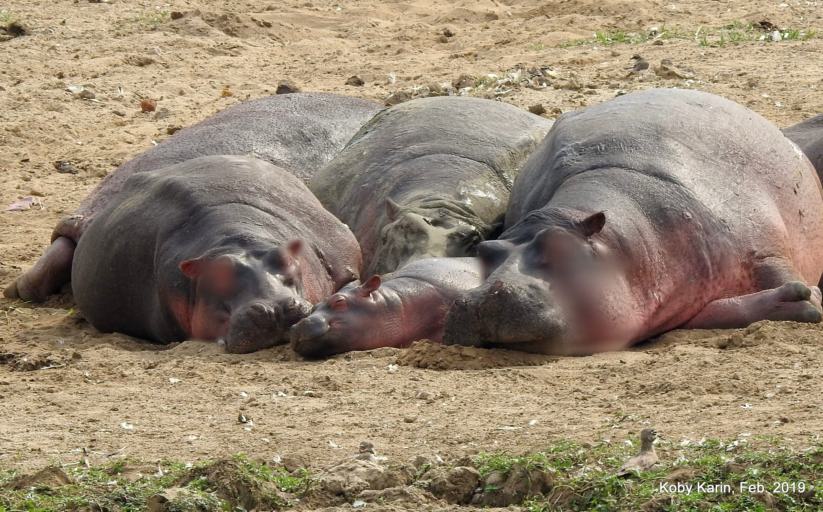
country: UG
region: Western Region
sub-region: Rubirizi District
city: Rubirizi
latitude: -0.2079
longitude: 29.8915
